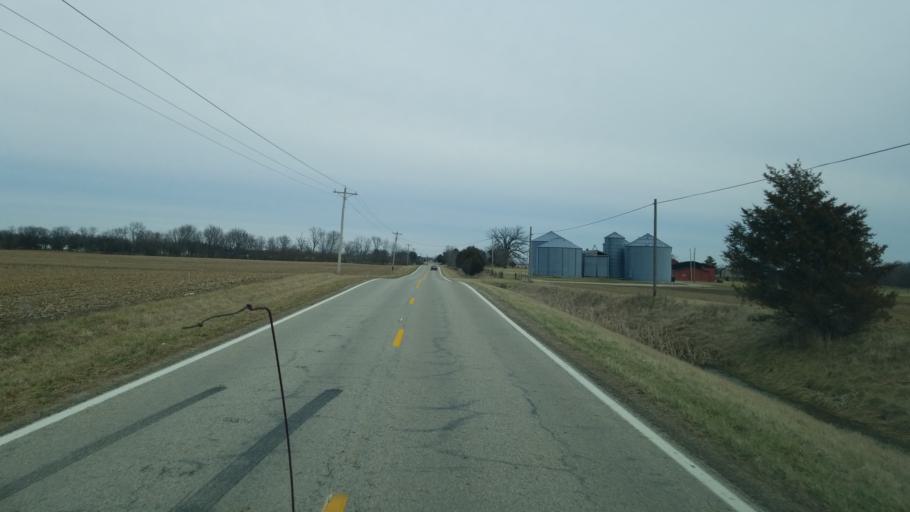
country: US
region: Ohio
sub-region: Pickaway County
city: Williamsport
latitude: 39.5656
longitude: -83.0746
